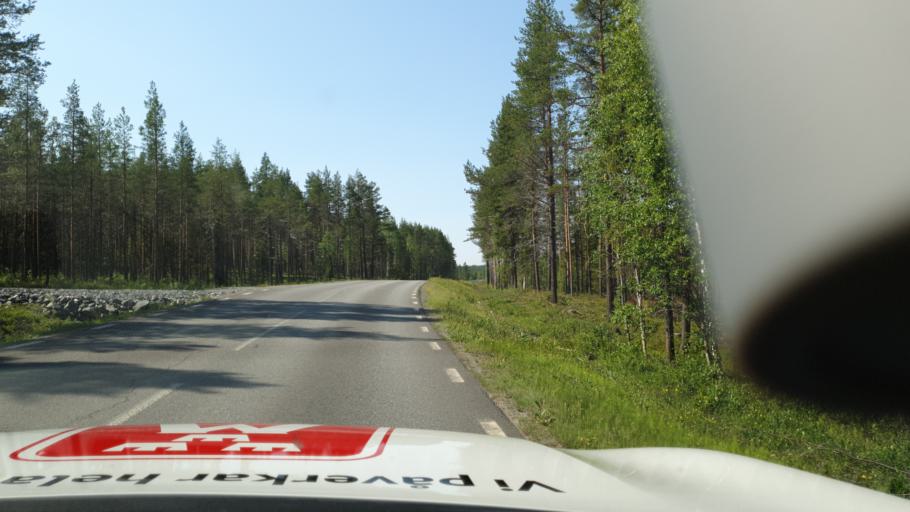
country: SE
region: Vaesterbotten
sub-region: Skelleftea Kommun
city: Langsele
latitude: 64.9522
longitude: 20.0306
